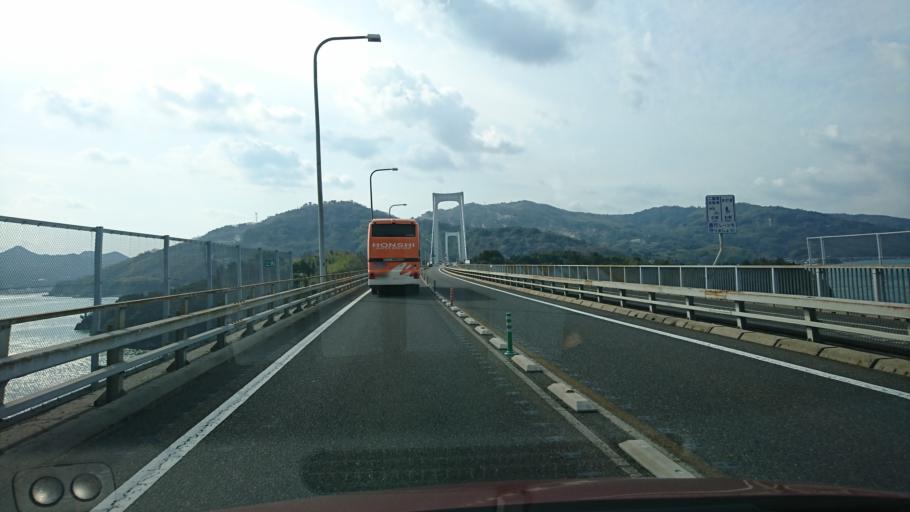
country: JP
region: Hiroshima
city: Innoshima
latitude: 34.1977
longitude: 133.0776
